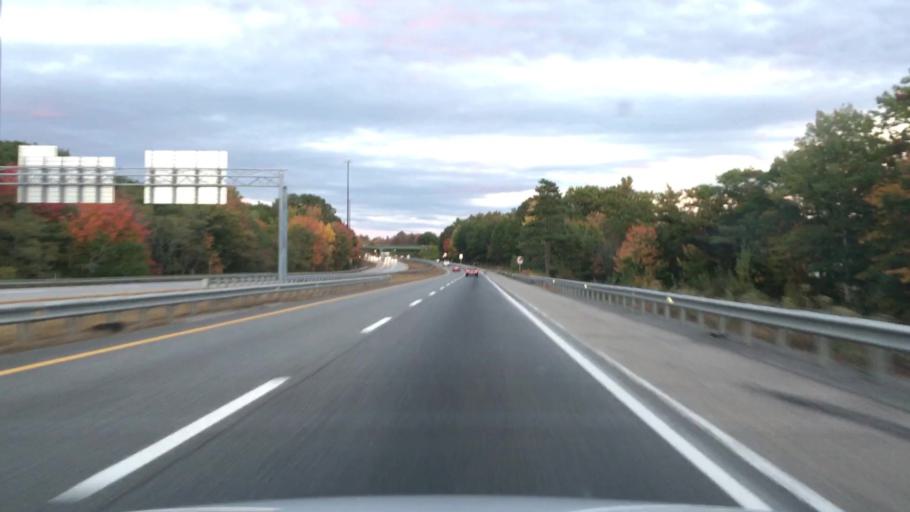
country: US
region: Maine
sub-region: Cumberland County
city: South Portland Gardens
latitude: 43.6274
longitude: -70.3251
